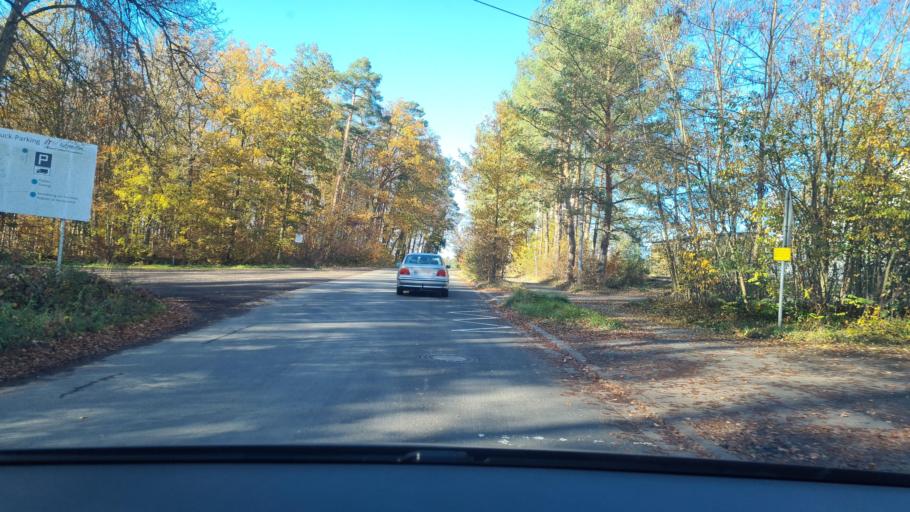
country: DE
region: Rheinland-Pfalz
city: Enkenbach-Alsenborn
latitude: 49.4830
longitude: 7.8870
